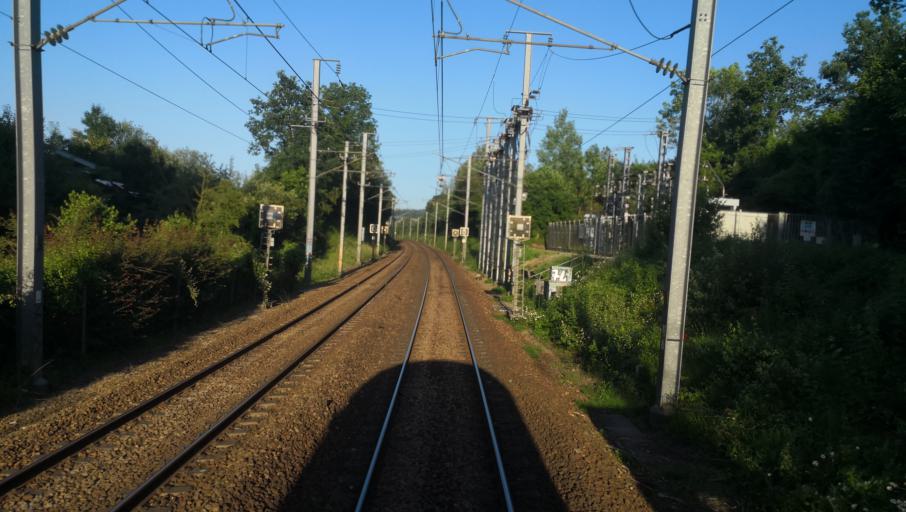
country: FR
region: Lower Normandy
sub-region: Departement du Calvados
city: Beuvillers
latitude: 49.1272
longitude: 0.2605
